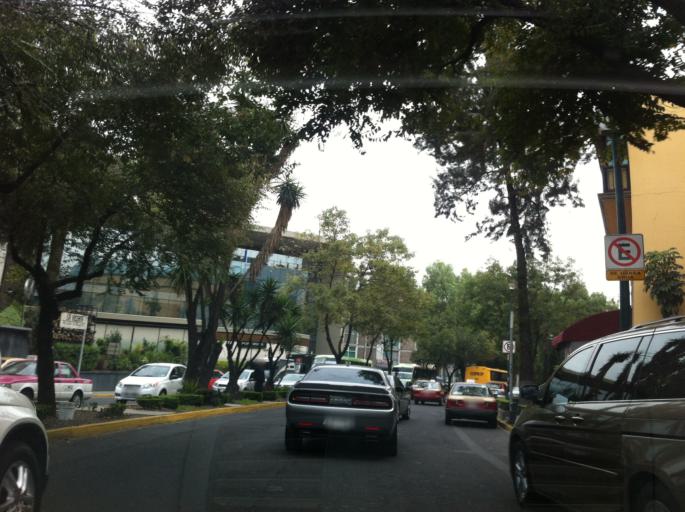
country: MX
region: Mexico City
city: Alvaro Obregon
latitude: 19.3488
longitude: -99.1903
